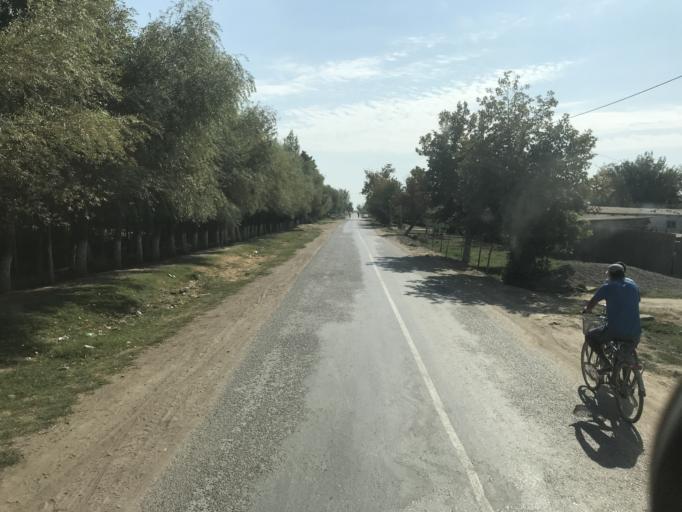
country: KZ
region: Ongtustik Qazaqstan
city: Myrzakent
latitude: 40.6643
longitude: 68.6208
